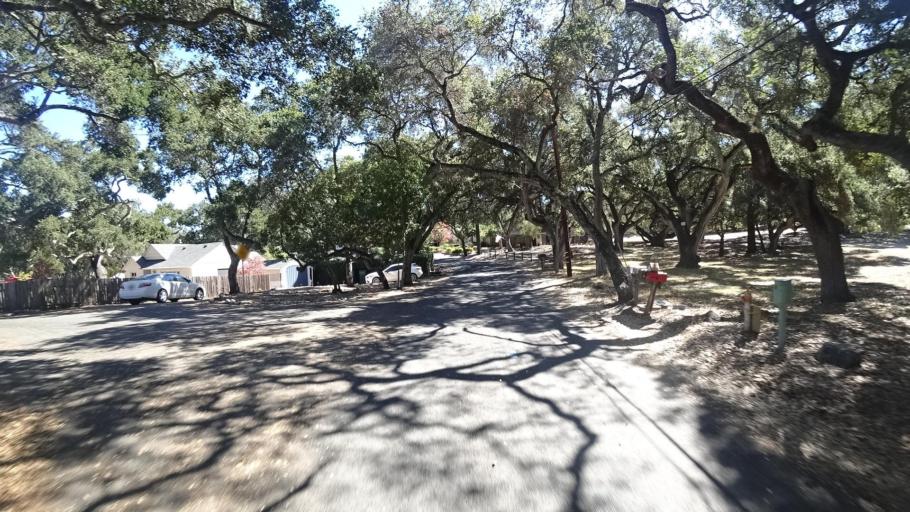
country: US
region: California
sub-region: Monterey County
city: Carmel Valley Village
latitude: 36.4698
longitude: -121.7308
